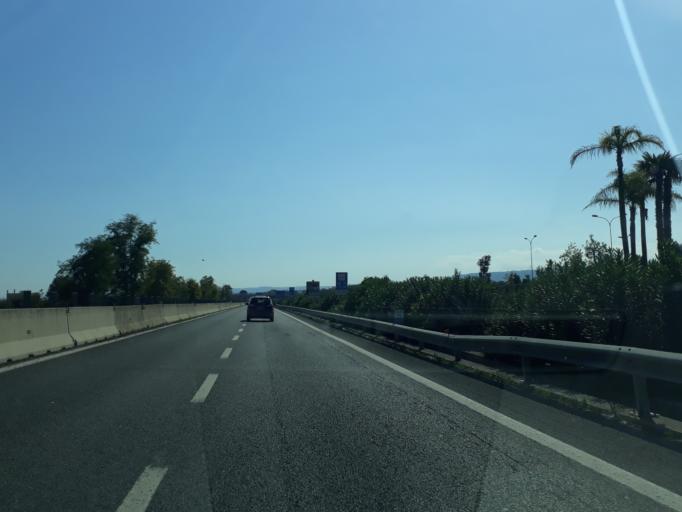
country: IT
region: Apulia
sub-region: Provincia di Bari
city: Monopoli
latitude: 40.9002
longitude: 17.3278
